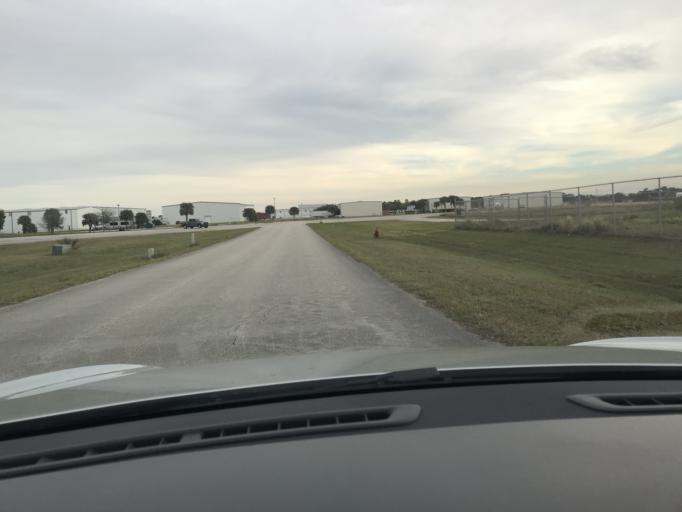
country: US
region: Florida
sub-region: Saint Lucie County
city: Lakewood Park
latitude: 27.4911
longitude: -80.3713
